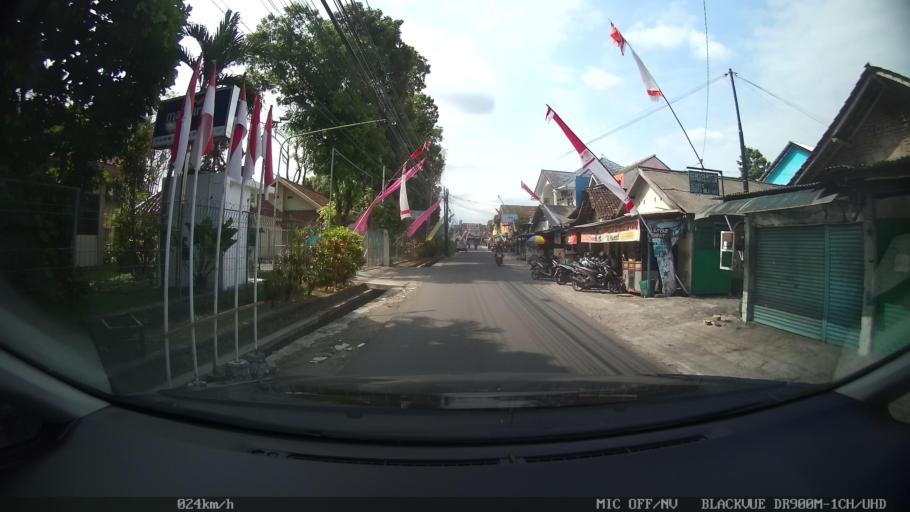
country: ID
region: Daerah Istimewa Yogyakarta
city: Depok
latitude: -7.7549
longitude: 110.4229
